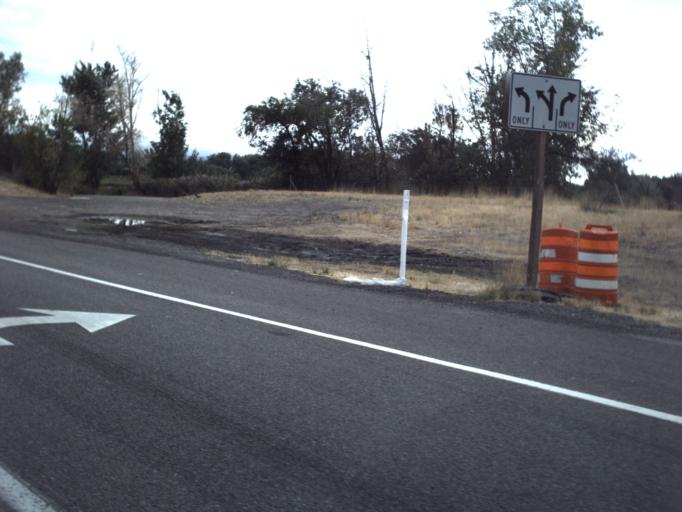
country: US
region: Utah
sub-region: Utah County
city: Springville
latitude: 40.1885
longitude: -111.6488
